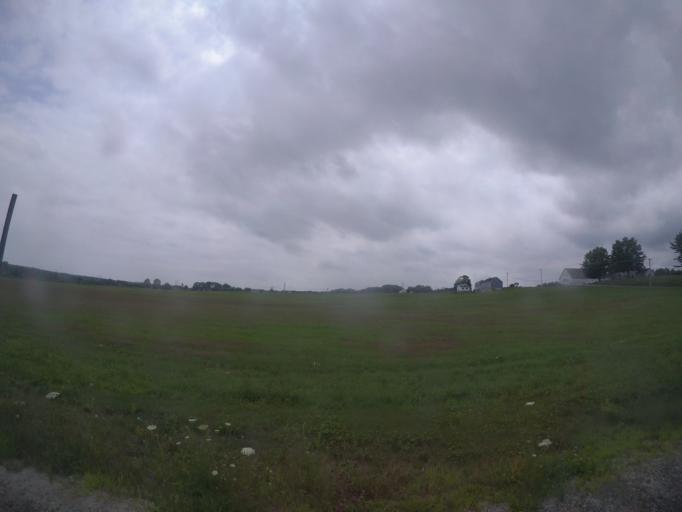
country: US
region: Maine
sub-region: Cumberland County
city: Cumberland Center
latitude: 43.7777
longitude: -70.2593
